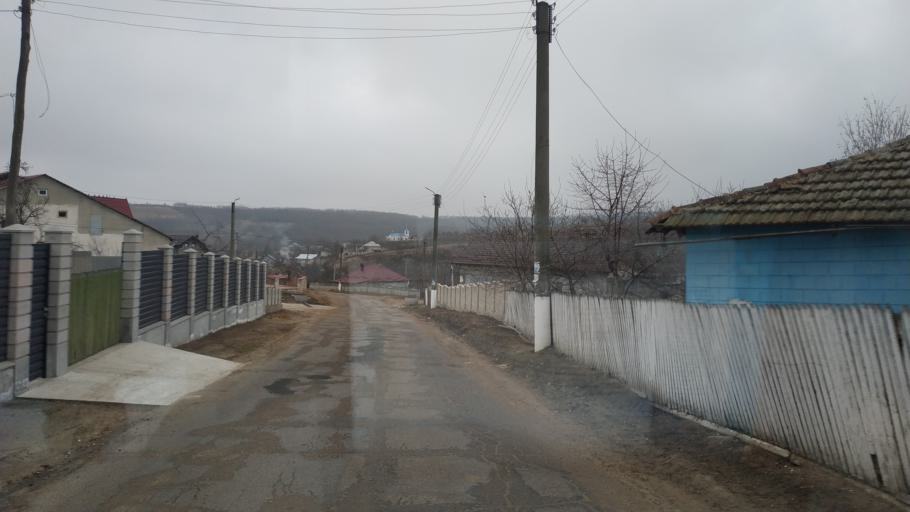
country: MD
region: Laloveni
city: Ialoveni
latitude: 46.8872
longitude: 28.6883
